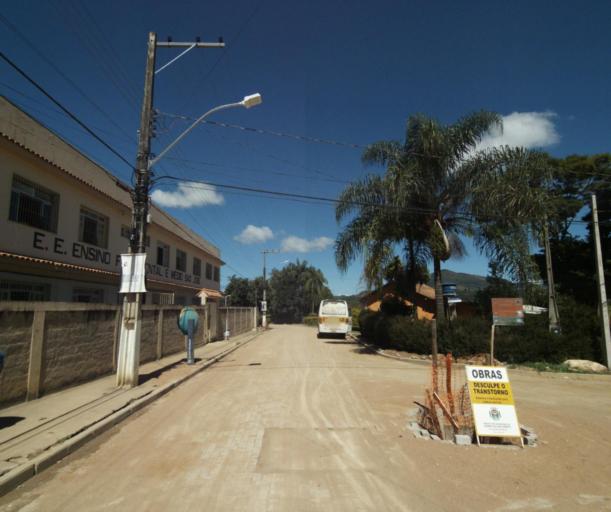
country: BR
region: Minas Gerais
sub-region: Espera Feliz
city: Espera Feliz
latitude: -20.5550
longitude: -41.8187
